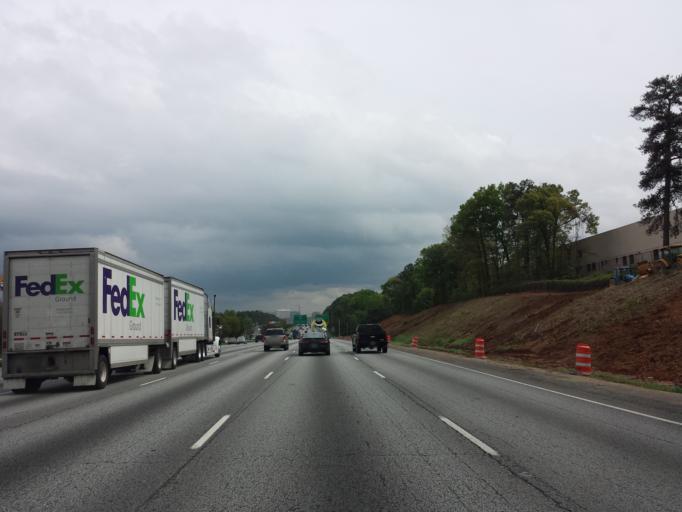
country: US
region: Georgia
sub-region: Cobb County
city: Smyrna
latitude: 33.9146
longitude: -84.4813
